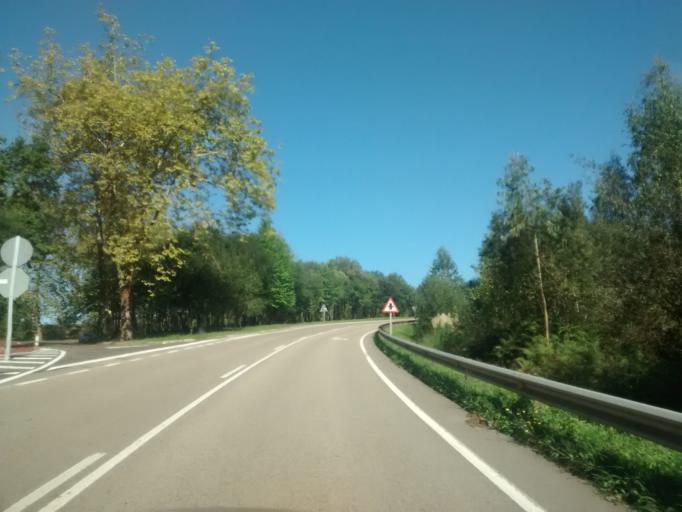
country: ES
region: Cantabria
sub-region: Provincia de Cantabria
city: Cabezon de la Sal
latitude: 43.3242
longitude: -4.2601
